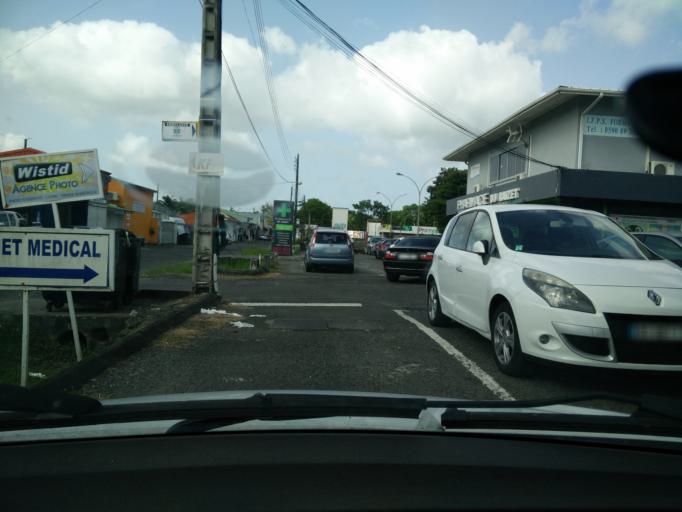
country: GP
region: Guadeloupe
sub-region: Guadeloupe
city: Pointe-a-Pitre
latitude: 16.2574
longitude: -61.5252
